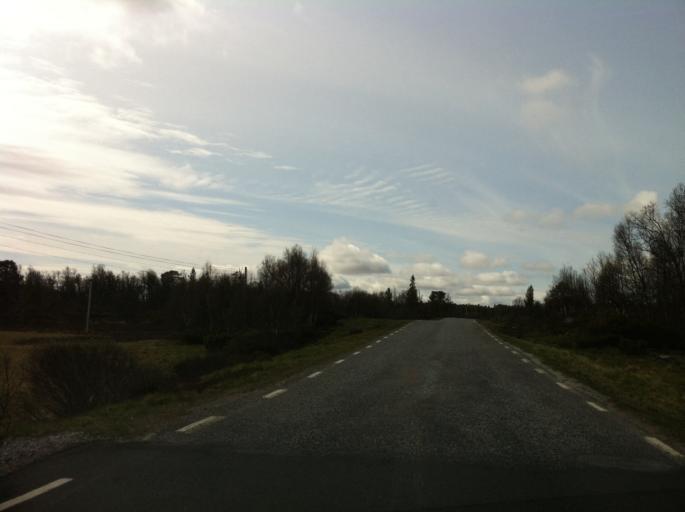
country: NO
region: Hedmark
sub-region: Engerdal
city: Engerdal
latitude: 62.3652
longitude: 12.7895
